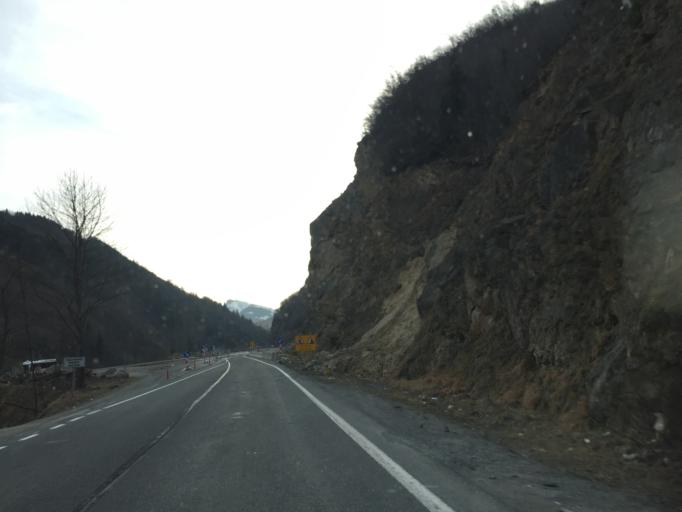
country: TR
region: Trabzon
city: Macka
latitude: 40.7338
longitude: 39.5370
